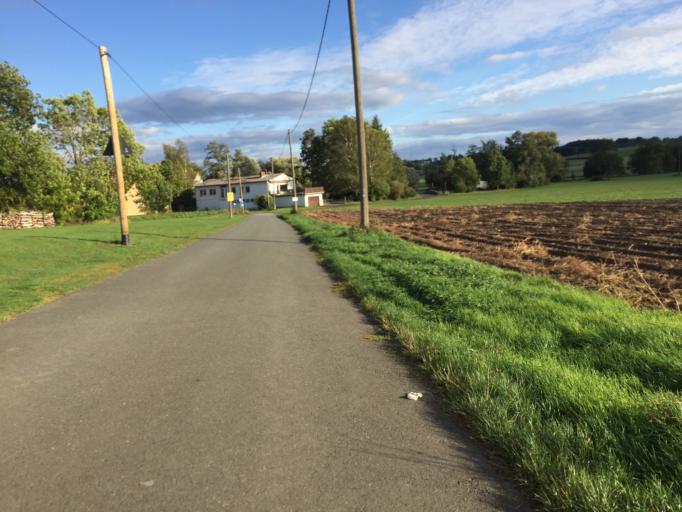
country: DE
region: Hesse
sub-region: Regierungsbezirk Darmstadt
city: Munzenberg
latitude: 50.4612
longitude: 8.7514
